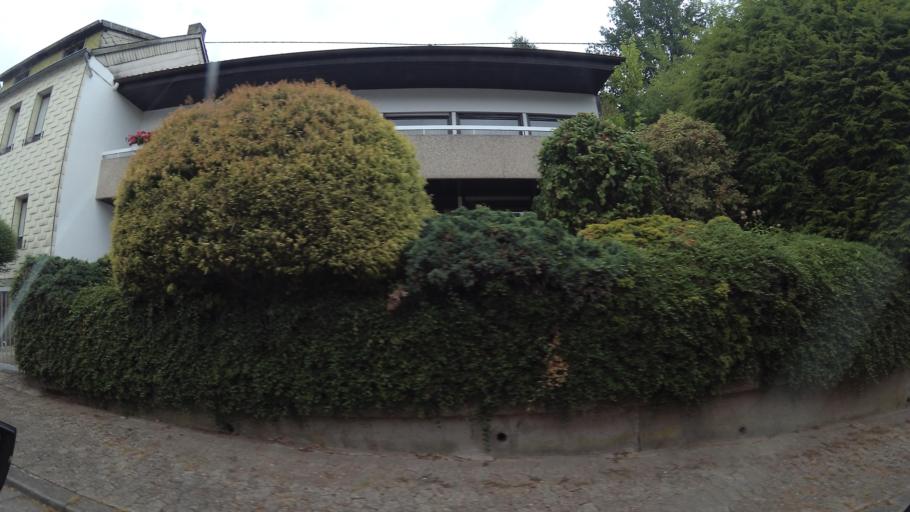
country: DE
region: Saarland
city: Spiesen-Elversberg
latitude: 49.3131
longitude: 7.1338
